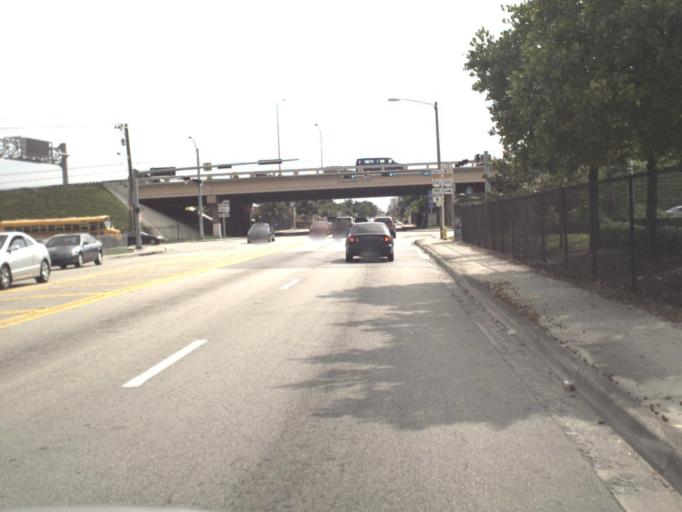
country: US
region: Florida
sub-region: Miami-Dade County
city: Brownsville
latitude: 25.7872
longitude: -80.2560
